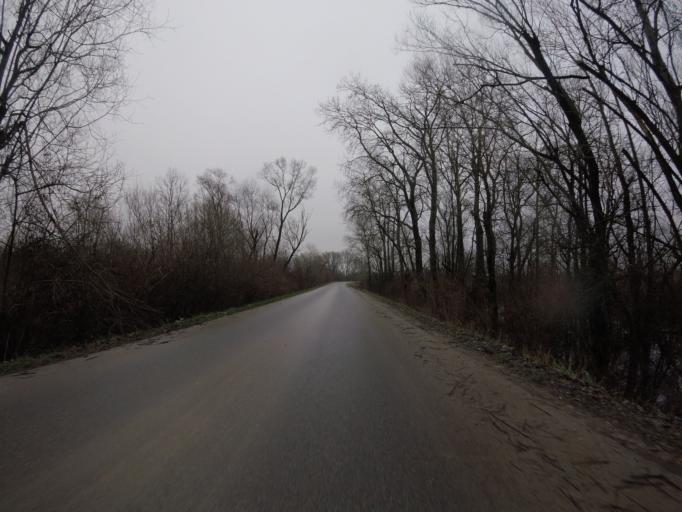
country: HR
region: Sisacko-Moslavacka
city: Lekenik
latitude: 45.6245
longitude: 16.3227
